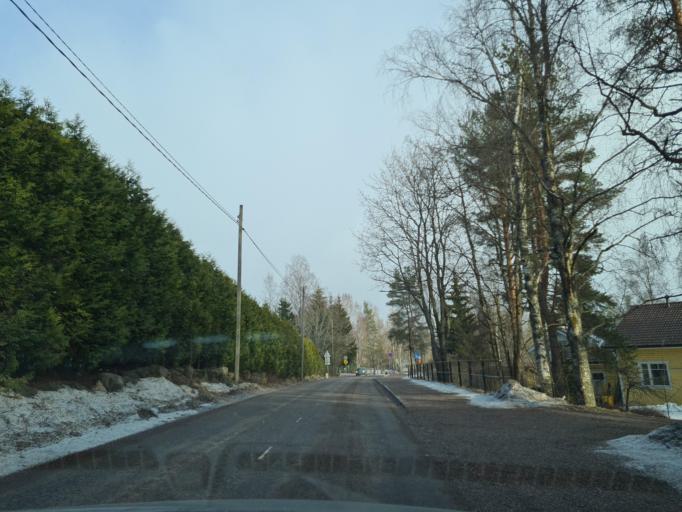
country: FI
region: Uusimaa
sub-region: Helsinki
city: Maentsaelae
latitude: 60.6395
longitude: 25.3128
